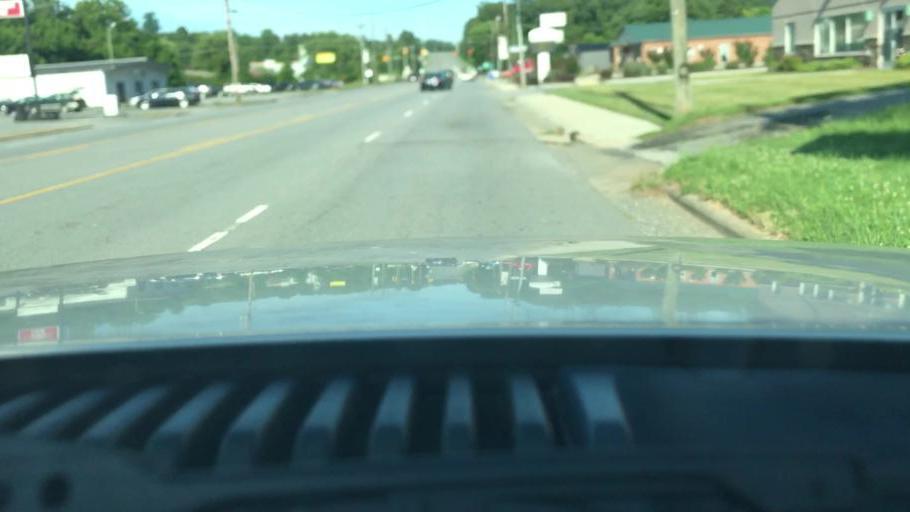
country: US
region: North Carolina
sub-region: Yadkin County
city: Jonesville
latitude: 36.2403
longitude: -80.8338
